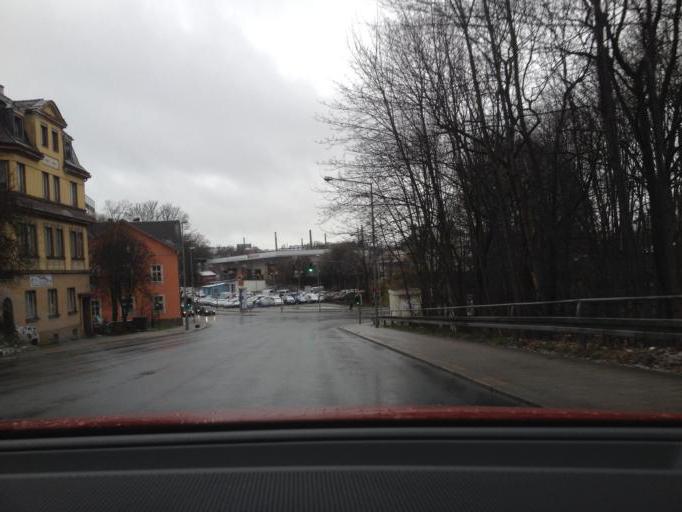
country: DE
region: Bavaria
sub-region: Upper Franconia
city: Hof
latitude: 50.3103
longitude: 11.9111
